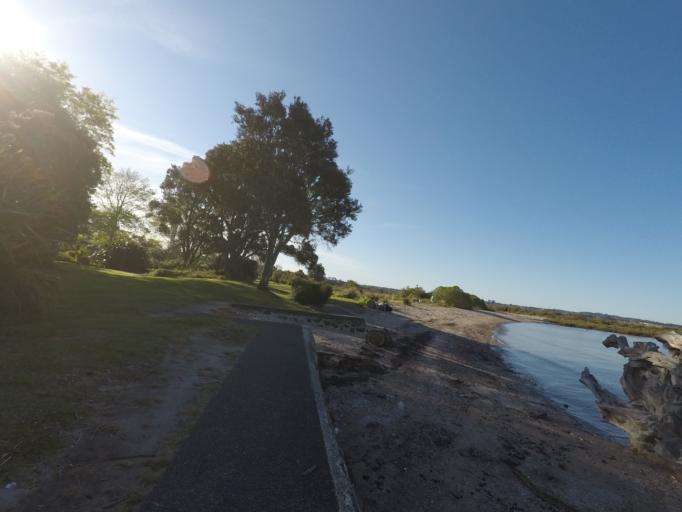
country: NZ
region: Auckland
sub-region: Auckland
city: Rosebank
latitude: -36.8281
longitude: 174.6548
